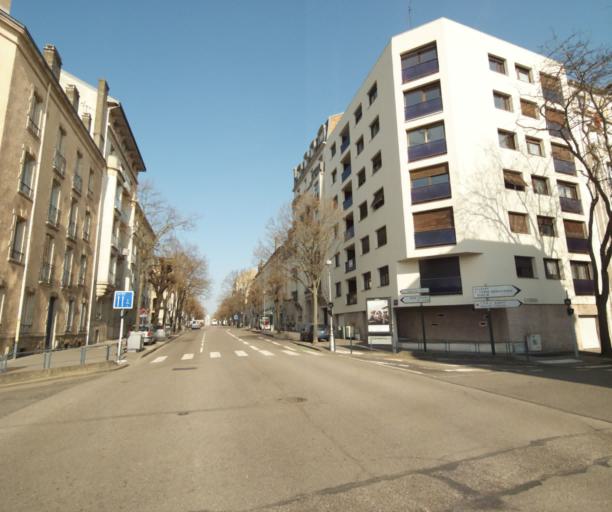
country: FR
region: Lorraine
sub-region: Departement de Meurthe-et-Moselle
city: Nancy
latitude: 48.6756
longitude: 6.1821
